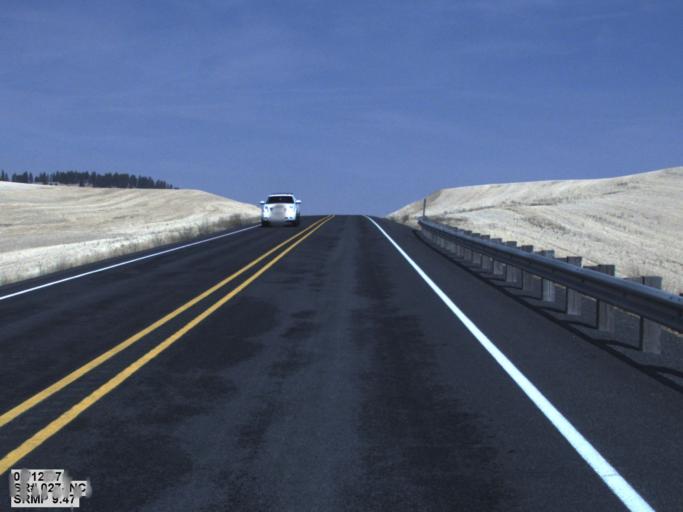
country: US
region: Washington
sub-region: Whitman County
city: Pullman
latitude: 46.8497
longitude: -117.1249
